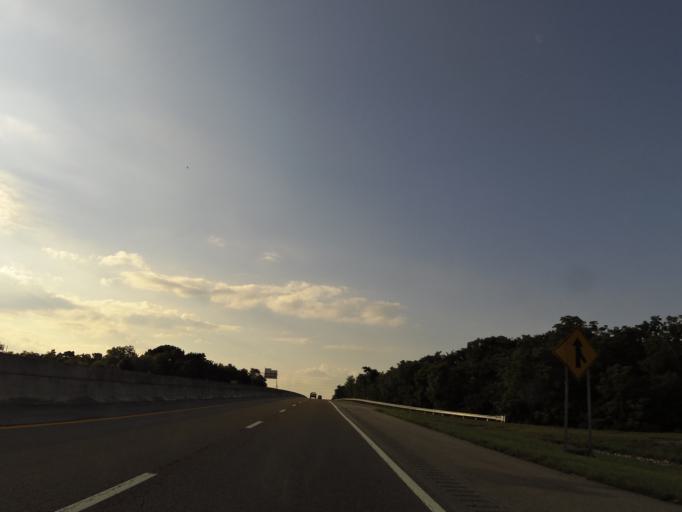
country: US
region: Tennessee
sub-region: Knox County
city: Farragut
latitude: 35.9008
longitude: -84.1177
